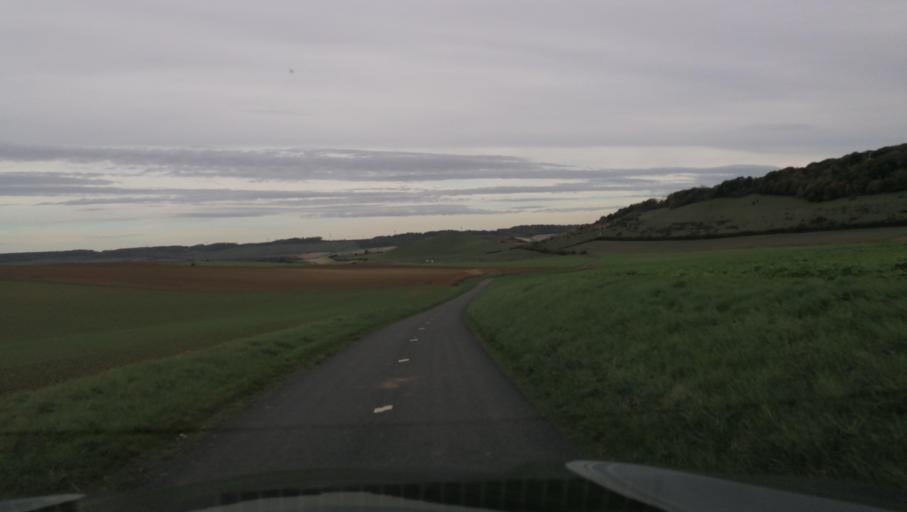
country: FR
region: Picardie
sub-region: Departement de la Somme
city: Bouttencourt
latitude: 49.8856
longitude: 1.6660
